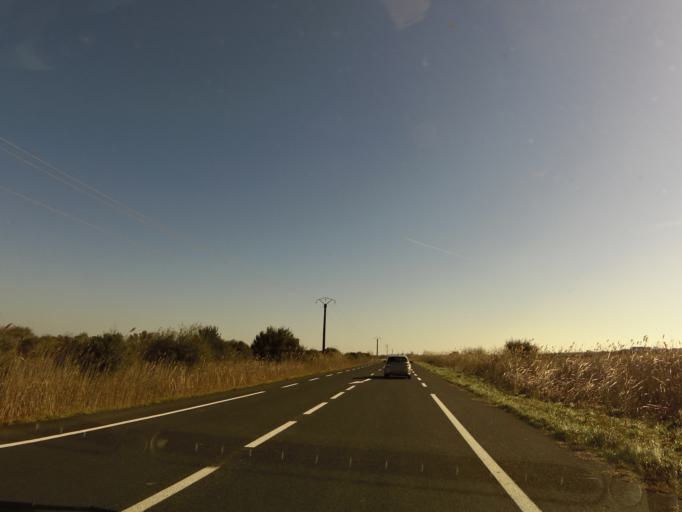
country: FR
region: Languedoc-Roussillon
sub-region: Departement du Gard
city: Aigues-Mortes
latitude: 43.5693
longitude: 4.3100
